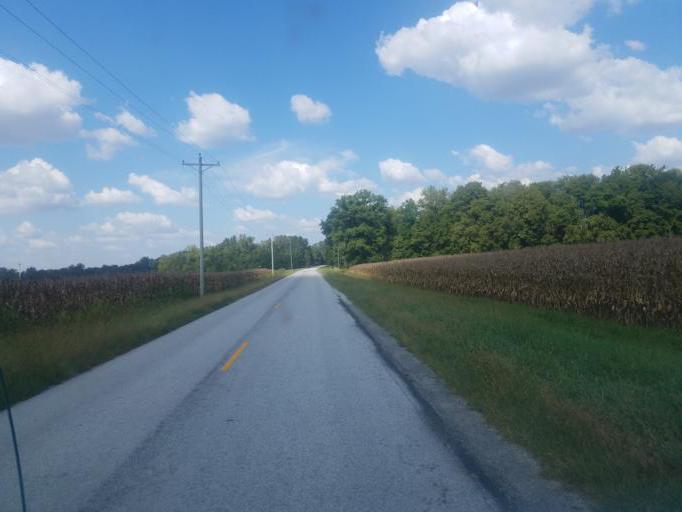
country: US
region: Ohio
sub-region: Auglaize County
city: Cridersville
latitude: 40.6532
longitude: -84.2512
